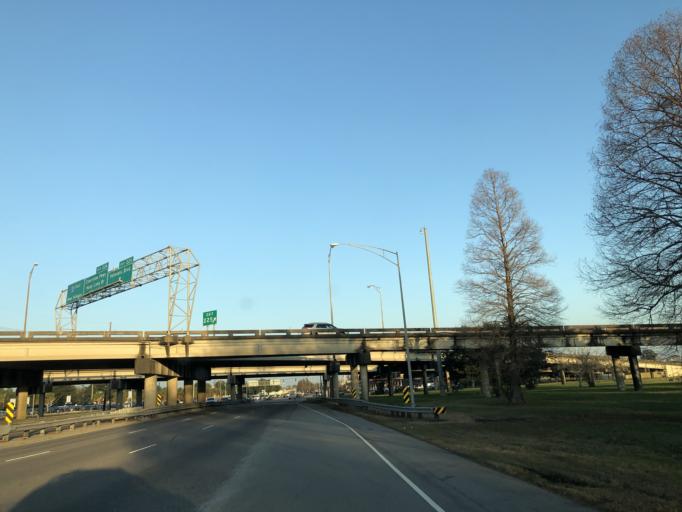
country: US
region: Louisiana
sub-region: Jefferson Parish
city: Kenner
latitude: 30.0050
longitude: -90.2095
